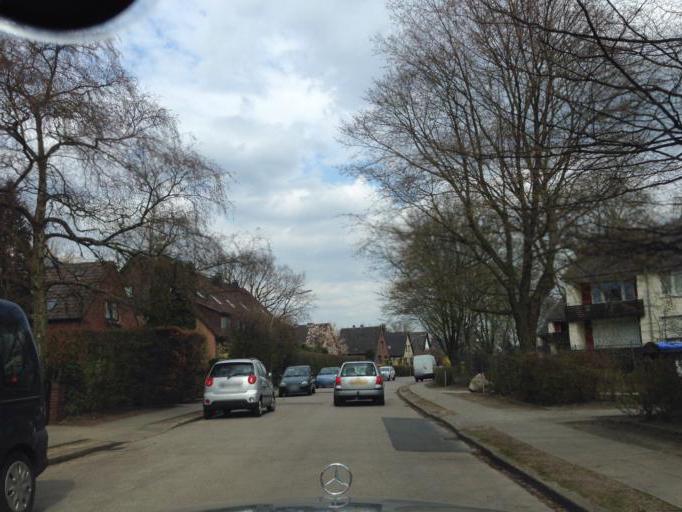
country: DE
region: Hamburg
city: Farmsen-Berne
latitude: 53.5861
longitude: 10.1357
